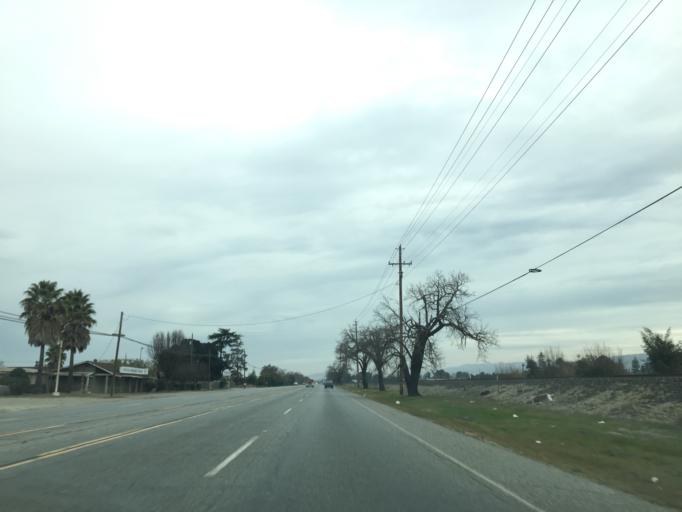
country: US
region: California
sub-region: Santa Clara County
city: San Martin
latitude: 37.0461
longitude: -121.5884
